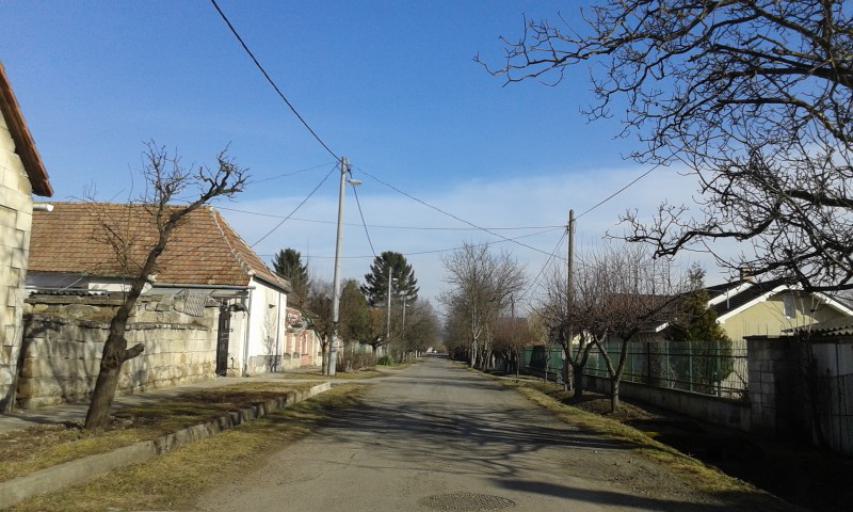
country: HU
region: Pest
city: Soskut
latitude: 47.4019
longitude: 18.8177
